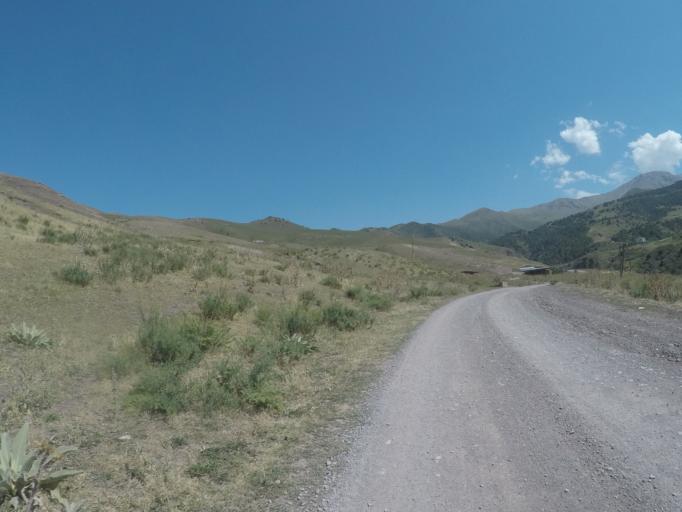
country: KG
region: Chuy
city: Bishkek
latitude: 42.6495
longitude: 74.5105
